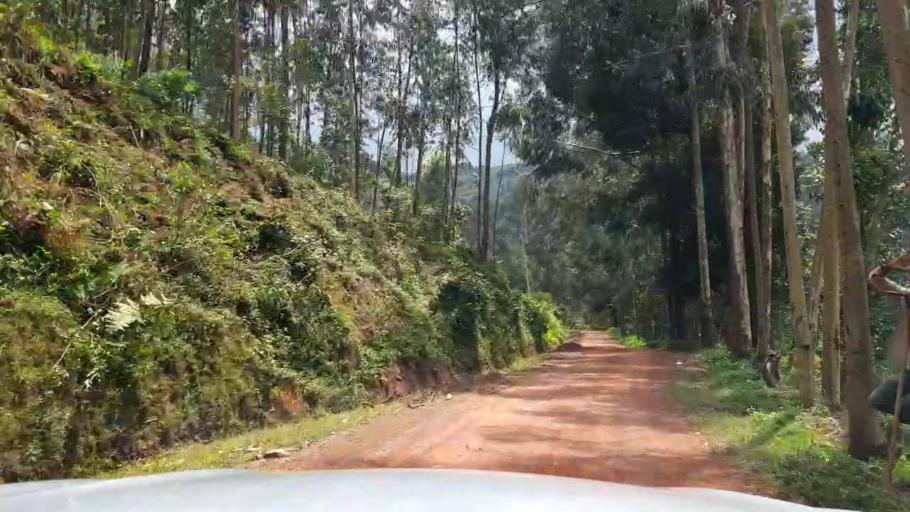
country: UG
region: Western Region
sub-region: Kabale District
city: Kabale
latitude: -1.4234
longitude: 29.8662
